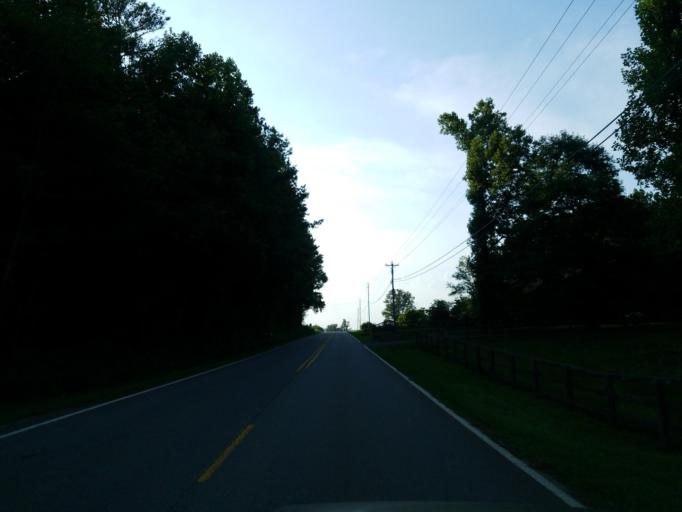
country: US
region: Georgia
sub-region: Pickens County
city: Jasper
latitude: 34.5356
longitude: -84.5325
